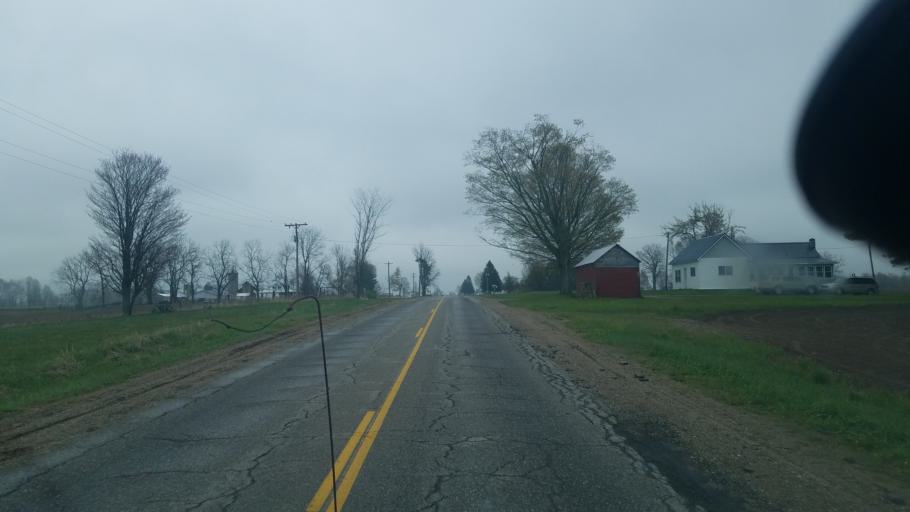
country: US
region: Michigan
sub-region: Mecosta County
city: Canadian Lakes
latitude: 43.5424
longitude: -85.3716
